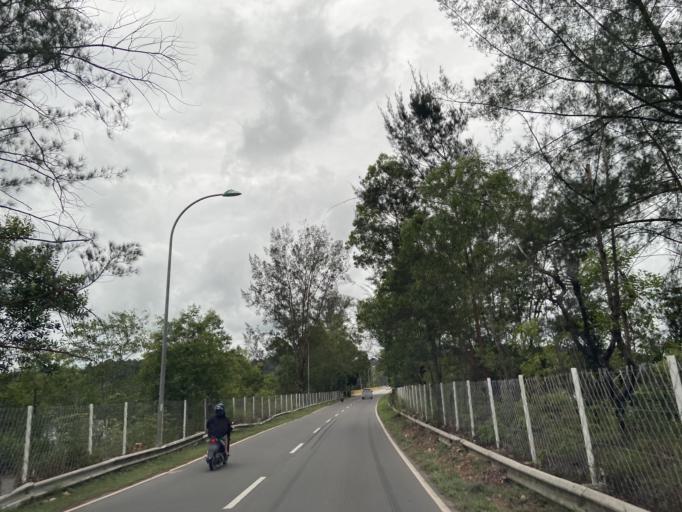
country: SG
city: Singapore
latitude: 1.1119
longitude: 104.0118
